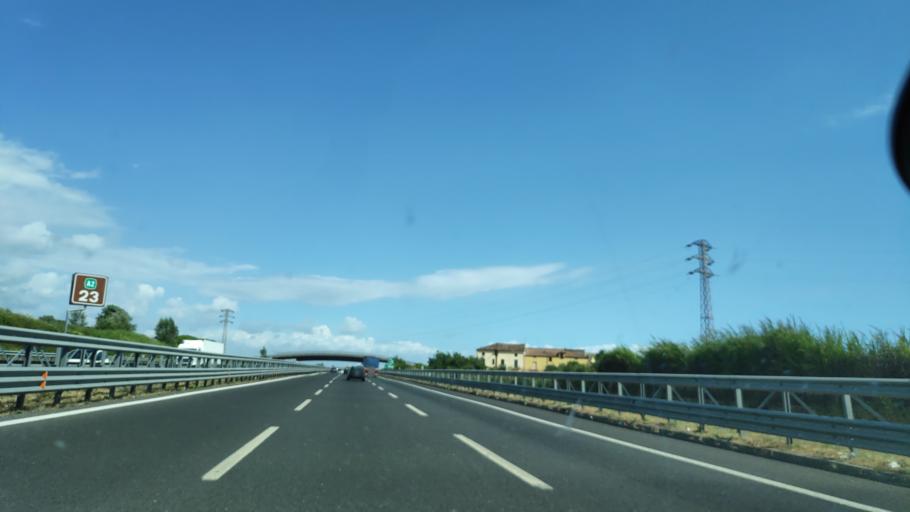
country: IT
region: Campania
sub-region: Provincia di Salerno
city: Pontecagnano
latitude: 40.6498
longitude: 14.8796
